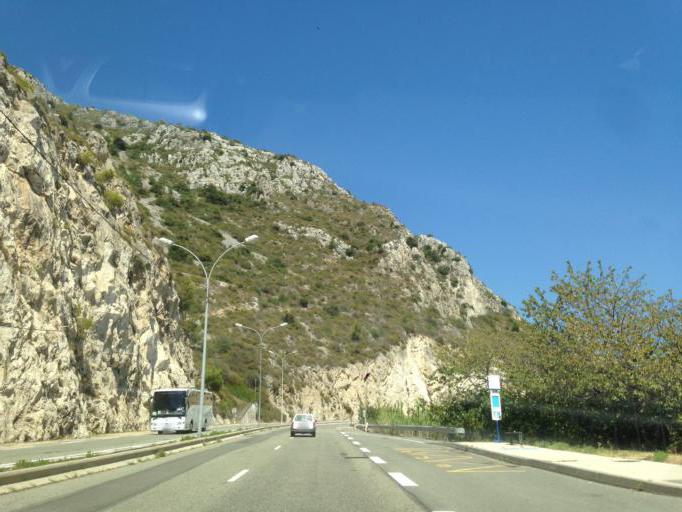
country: FR
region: Provence-Alpes-Cote d'Azur
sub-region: Departement des Alpes-Maritimes
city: Eze
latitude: 43.7263
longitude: 7.3490
